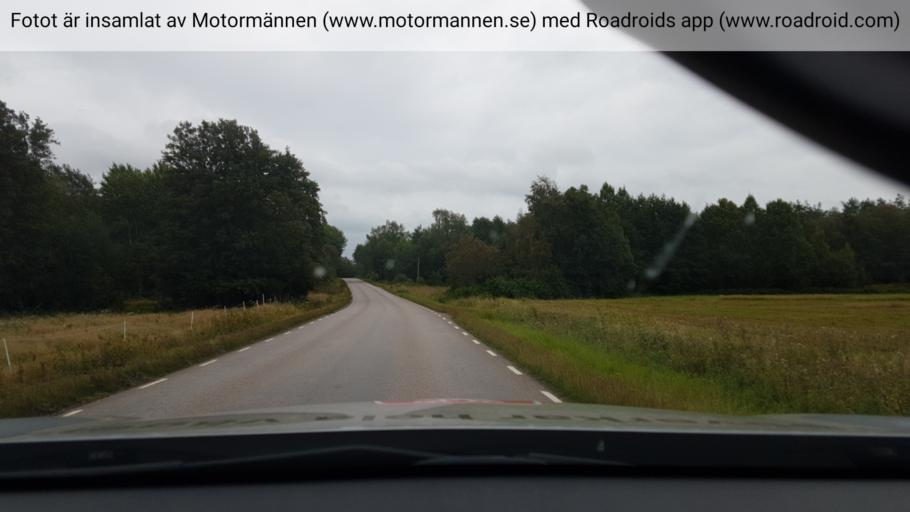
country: SE
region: Vaestra Goetaland
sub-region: Tanums Kommun
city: Grebbestad
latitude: 58.6746
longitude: 11.2856
